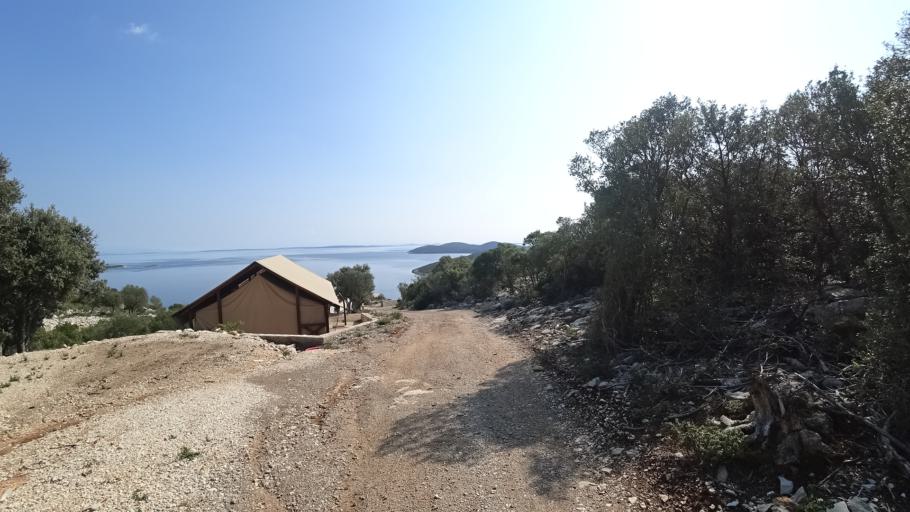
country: HR
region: Primorsko-Goranska
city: Mali Losinj
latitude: 44.4869
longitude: 14.5362
